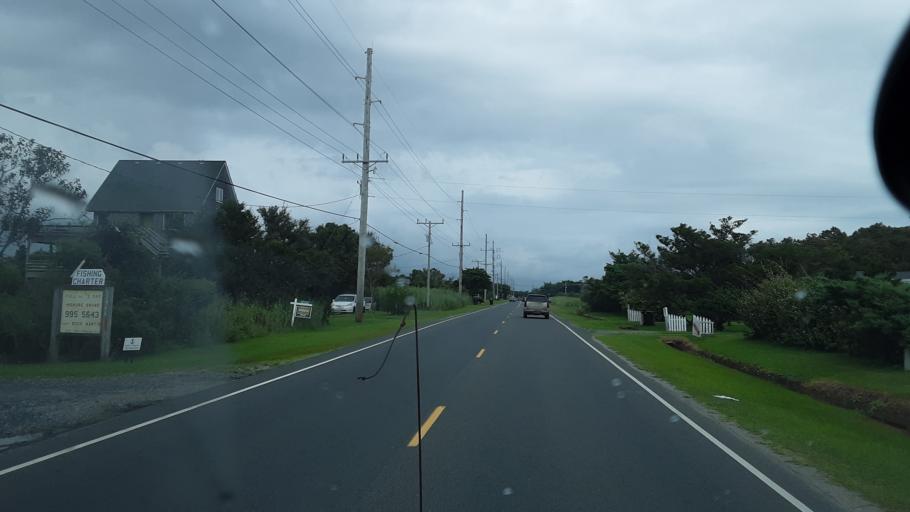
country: US
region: North Carolina
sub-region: Dare County
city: Buxton
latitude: 35.2357
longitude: -75.6234
